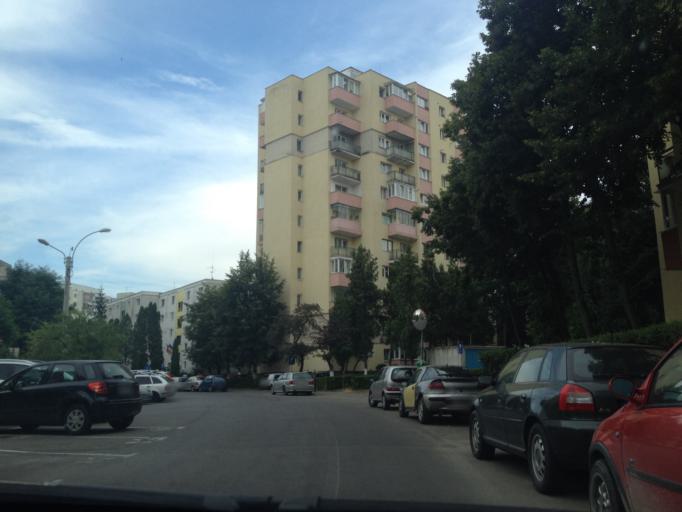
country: RO
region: Cluj
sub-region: Municipiul Cluj-Napoca
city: Cluj-Napoca
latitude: 46.7521
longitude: 23.5502
